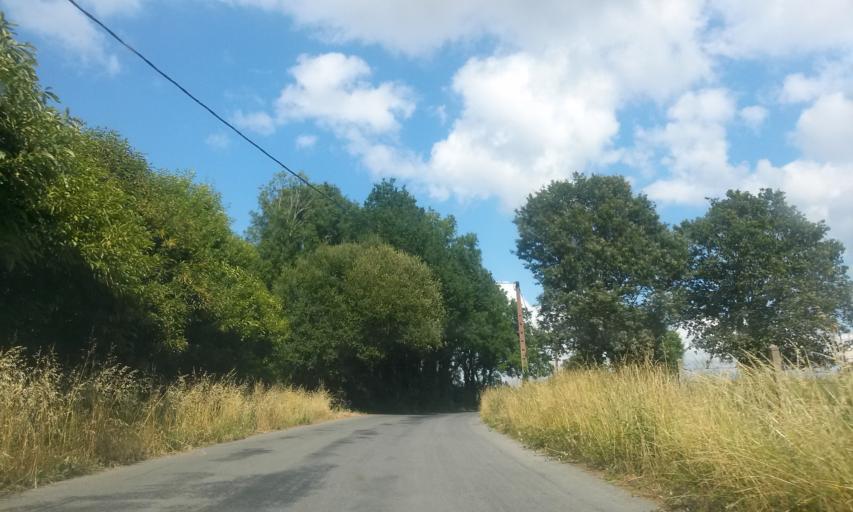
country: ES
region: Galicia
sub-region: Provincia de Lugo
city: Rabade
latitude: 43.1165
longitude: -7.6495
